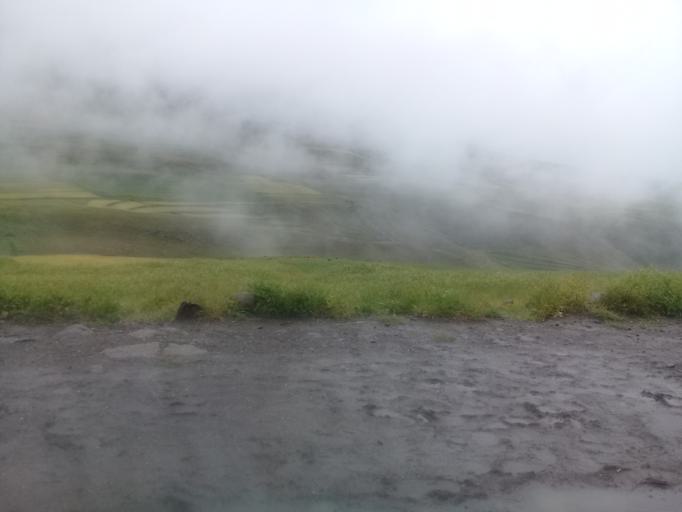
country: LS
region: Mokhotlong
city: Mokhotlong
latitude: -29.3818
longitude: 28.9813
